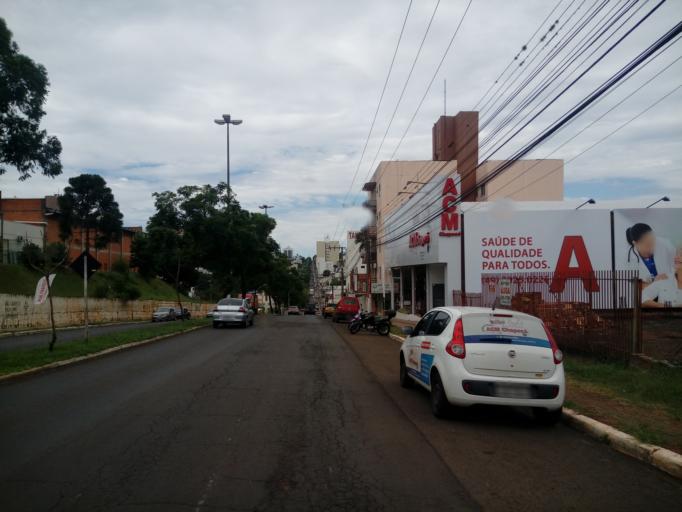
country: BR
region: Santa Catarina
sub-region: Chapeco
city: Chapeco
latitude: -27.0978
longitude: -52.6214
